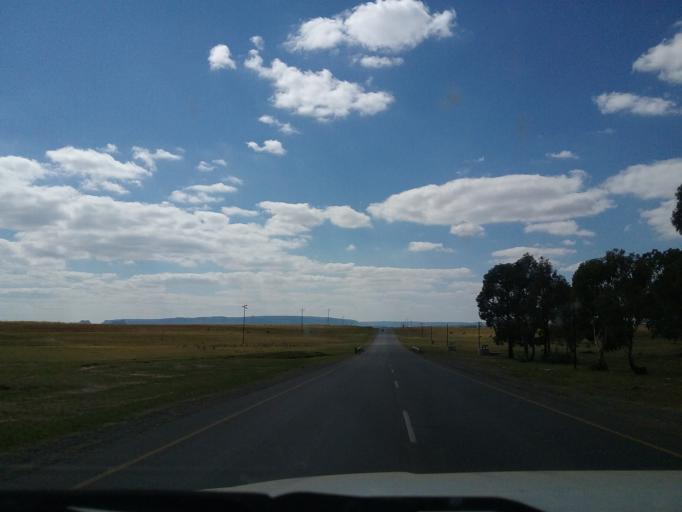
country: LS
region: Maseru
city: Maseru
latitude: -29.4785
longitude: 27.5289
